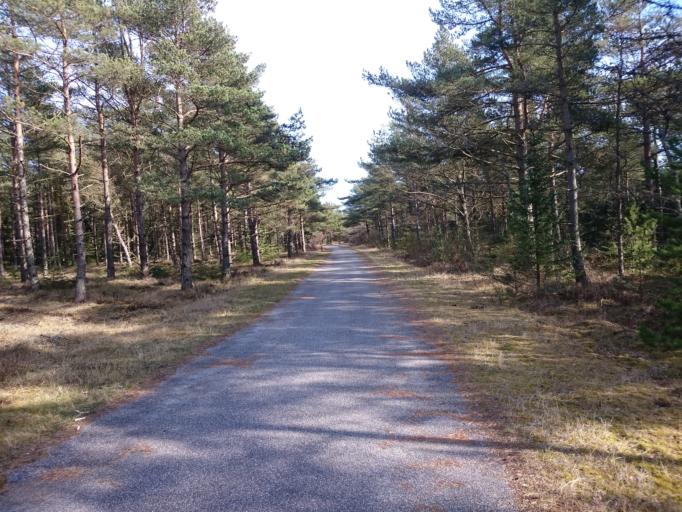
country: DK
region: North Denmark
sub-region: Frederikshavn Kommune
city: Skagen
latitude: 57.7004
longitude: 10.5169
